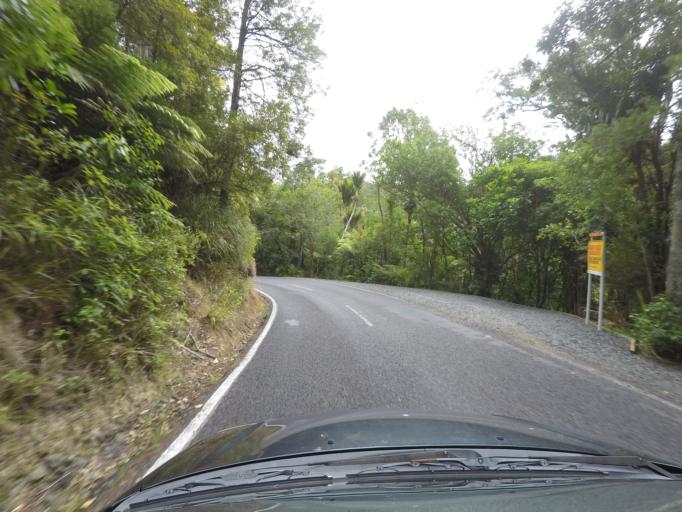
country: NZ
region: Auckland
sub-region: Auckland
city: Titirangi
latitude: -36.9475
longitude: 174.6583
